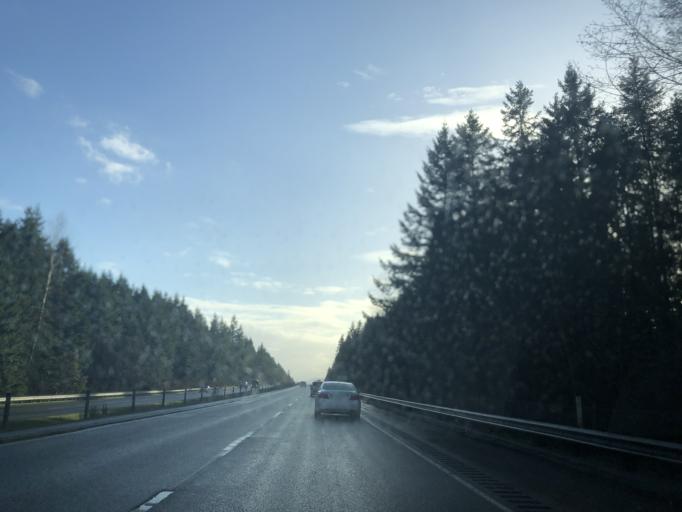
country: US
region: Washington
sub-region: Kitsap County
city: Bangor Trident Base
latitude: 47.7159
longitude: -122.6805
